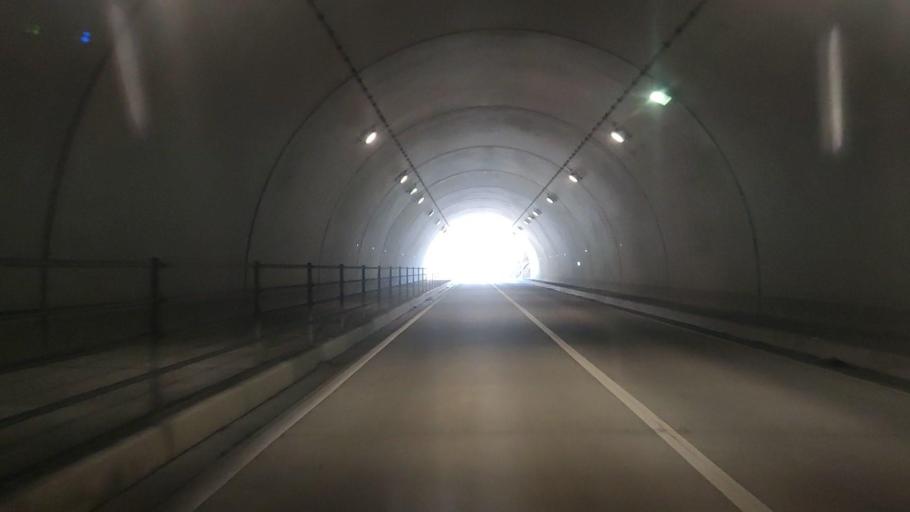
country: JP
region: Oita
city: Saiki
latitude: 32.8047
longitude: 131.8977
